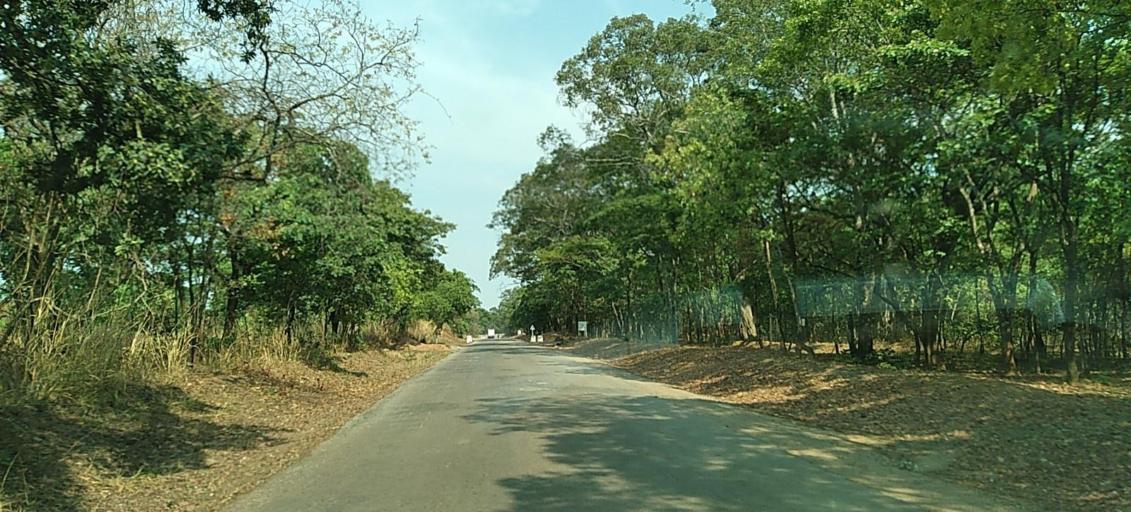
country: ZM
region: Copperbelt
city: Chililabombwe
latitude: -12.3044
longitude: 27.7830
